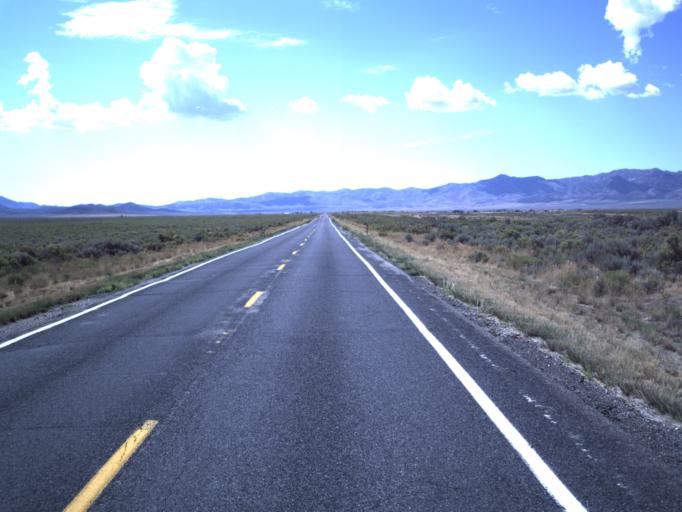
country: US
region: Utah
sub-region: Tooele County
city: Tooele
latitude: 40.1529
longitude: -112.4308
